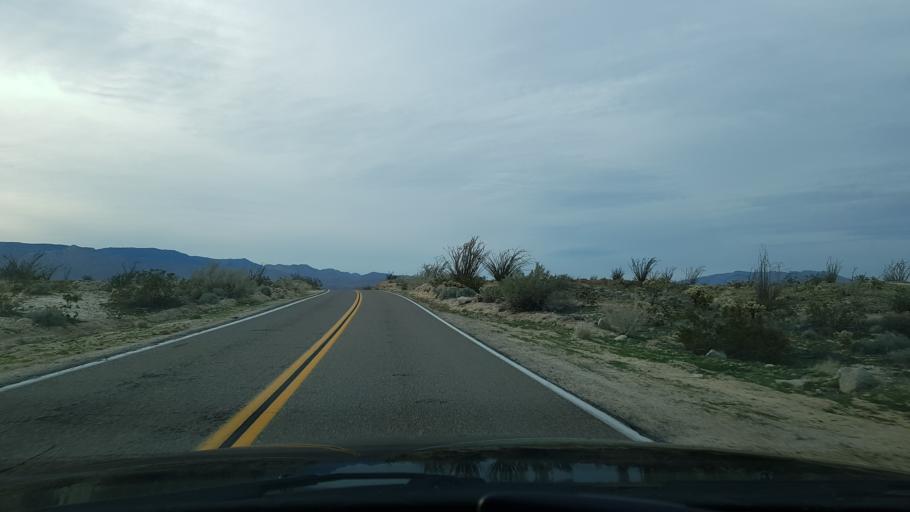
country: MX
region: Baja California
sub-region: Tecate
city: Cereso del Hongo
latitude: 32.8199
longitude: -116.1507
